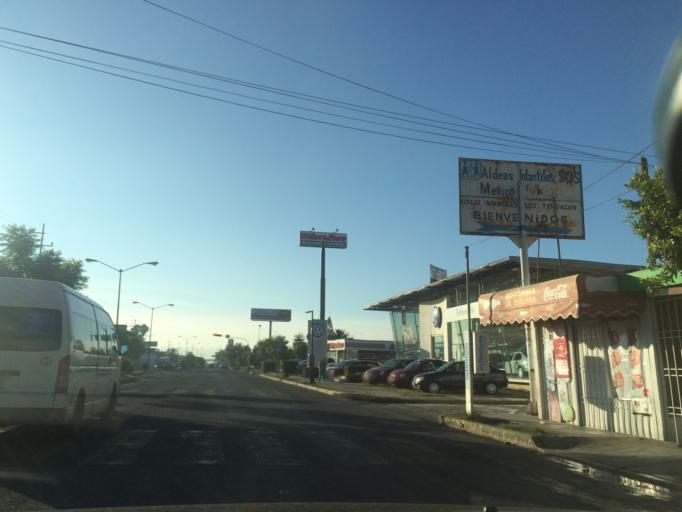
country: MX
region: Puebla
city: Tehuacan
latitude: 18.4675
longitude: -97.4183
